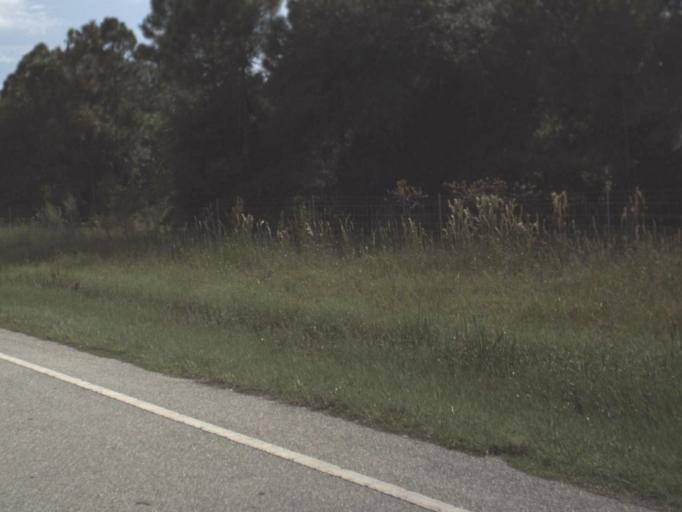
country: US
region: Florida
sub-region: Sarasota County
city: Plantation
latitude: 27.0782
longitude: -82.3299
